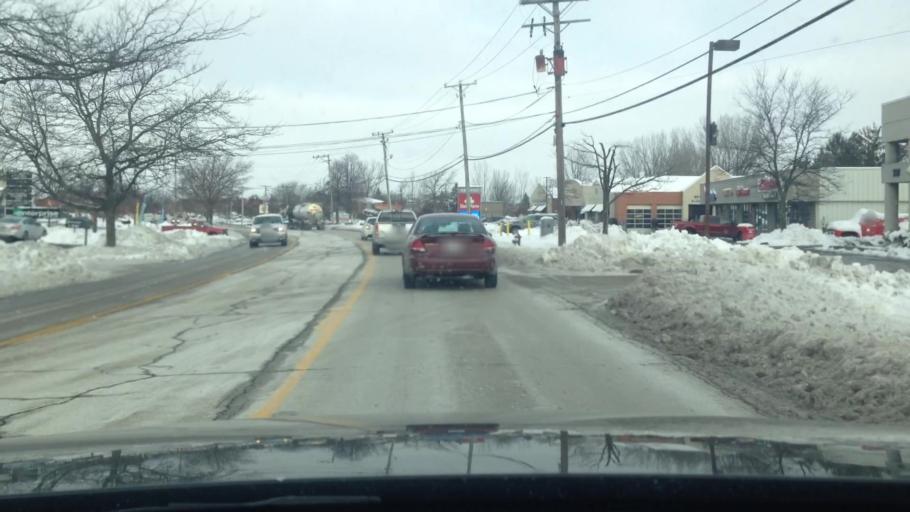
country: US
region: Illinois
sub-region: McHenry County
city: Woodstock
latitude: 42.3077
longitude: -88.4314
